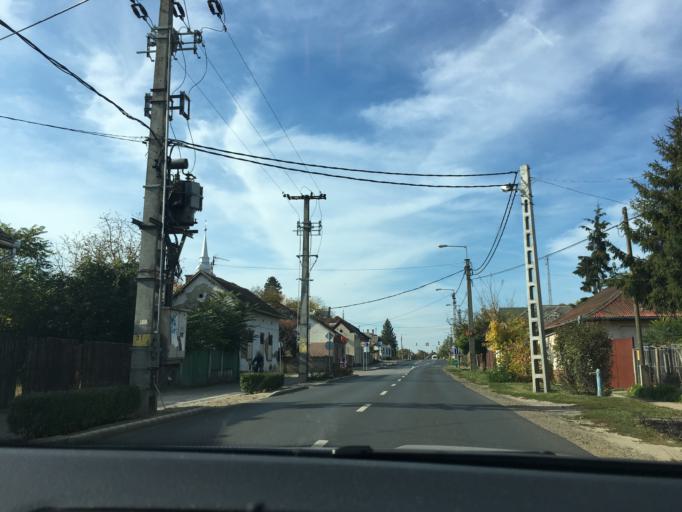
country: HU
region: Hajdu-Bihar
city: Vamospercs
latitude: 47.5256
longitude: 21.9006
